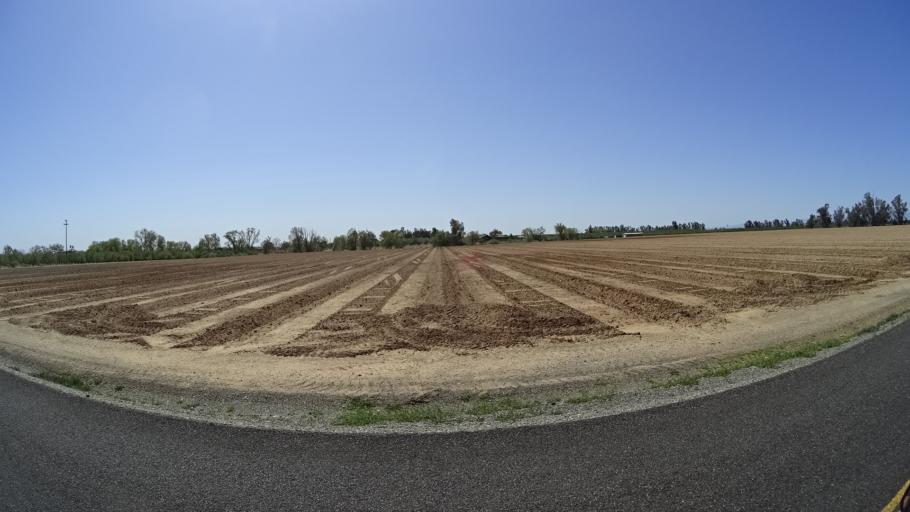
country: US
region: California
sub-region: Glenn County
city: Hamilton City
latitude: 39.7899
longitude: -122.0678
